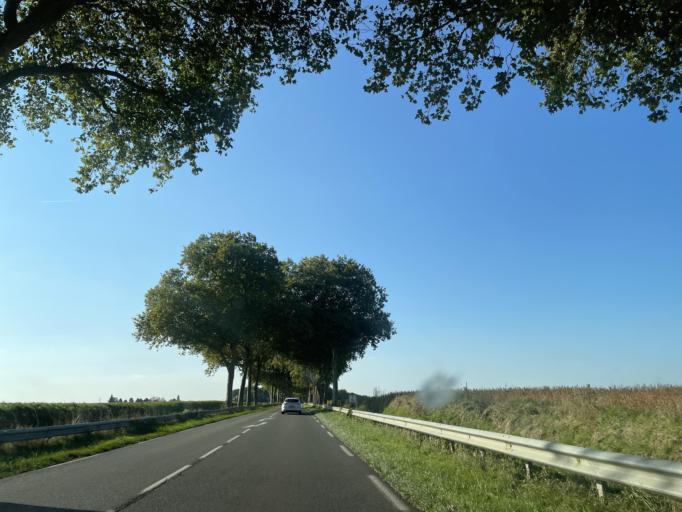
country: FR
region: Ile-de-France
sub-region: Departement de Seine-et-Marne
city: Guerard
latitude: 48.8398
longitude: 2.9658
